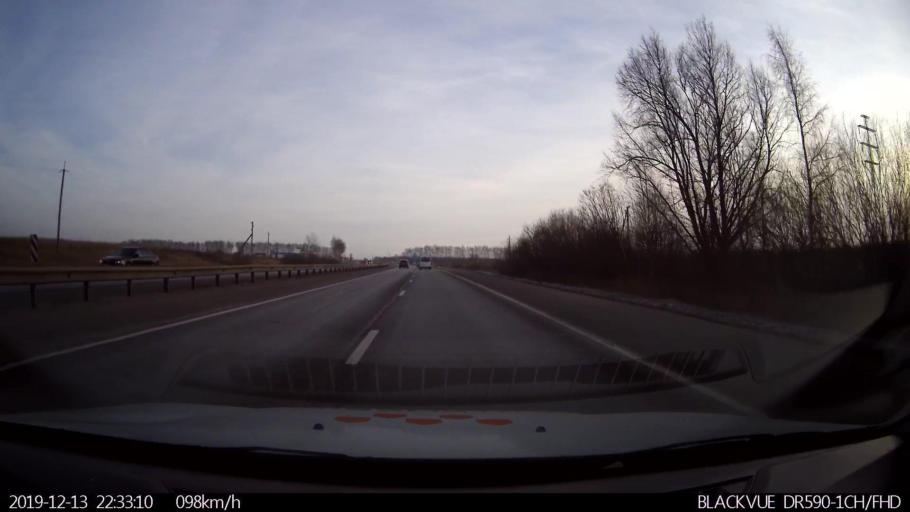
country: RU
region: Nizjnij Novgorod
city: Afonino
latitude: 56.1990
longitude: 44.1071
